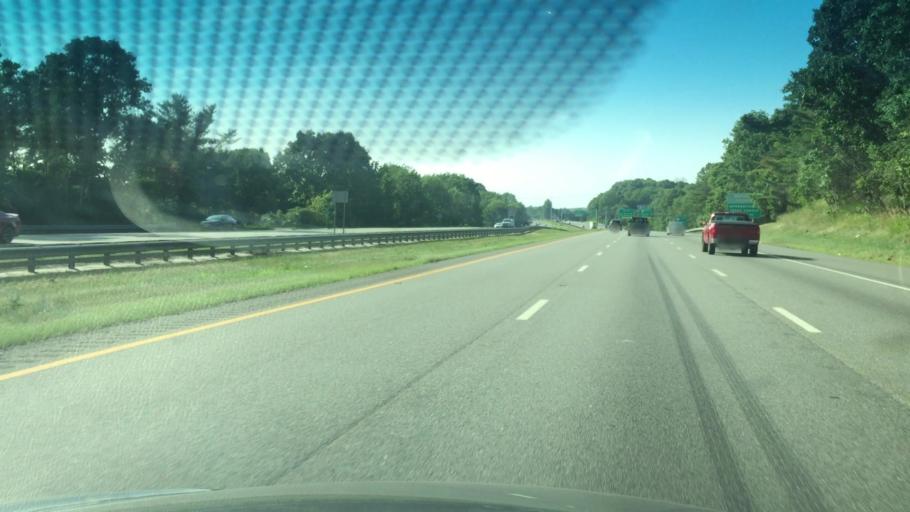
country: US
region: New Jersey
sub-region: Sussex County
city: Stanhope
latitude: 40.8980
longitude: -74.7182
